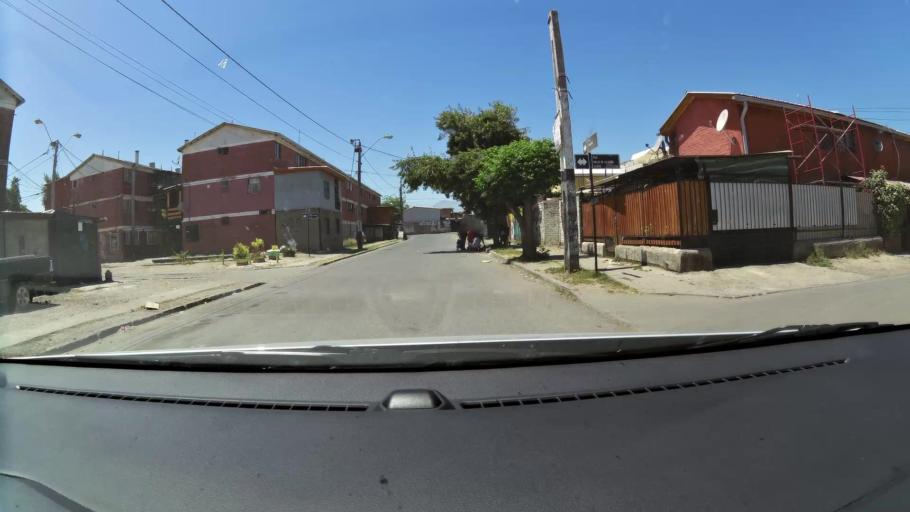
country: CL
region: Santiago Metropolitan
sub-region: Provincia de Santiago
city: La Pintana
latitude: -33.5786
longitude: -70.6646
